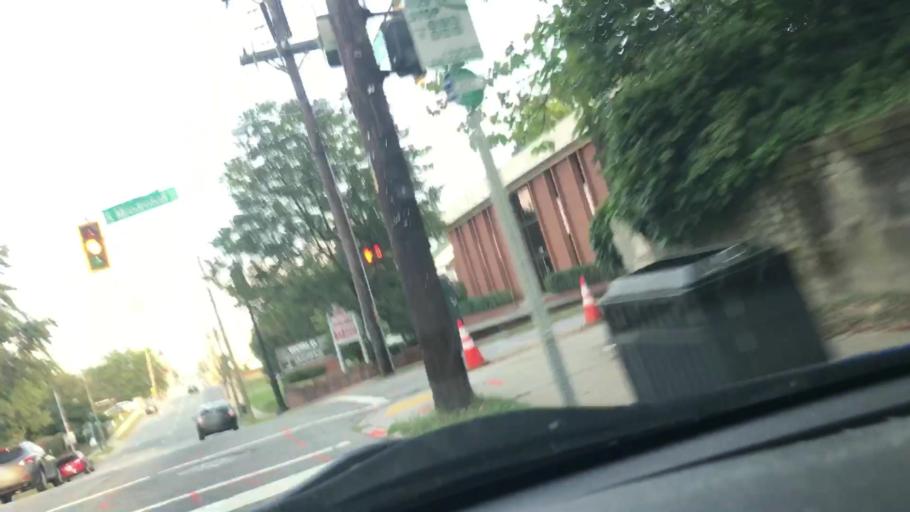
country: US
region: North Carolina
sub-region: Guilford County
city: Greensboro
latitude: 36.0732
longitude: -79.8042
